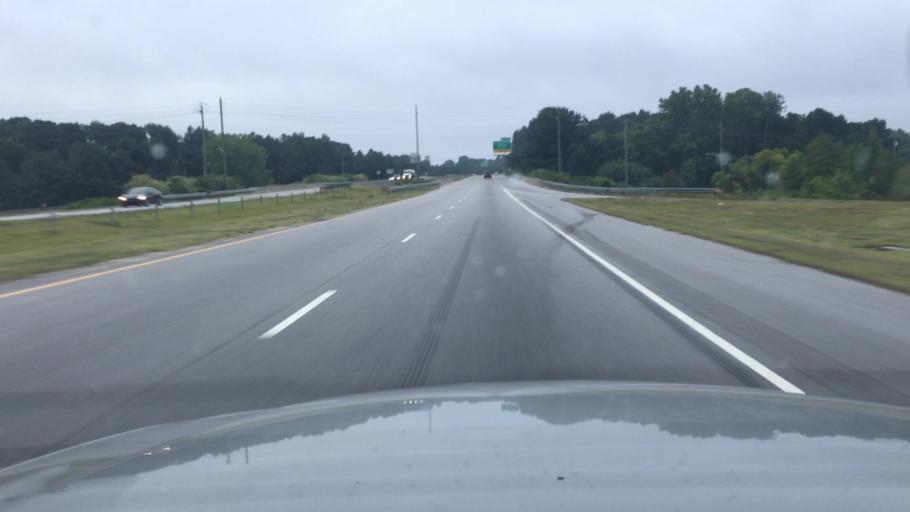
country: US
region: North Carolina
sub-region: Cumberland County
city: Fayetteville
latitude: 35.0460
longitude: -78.8935
